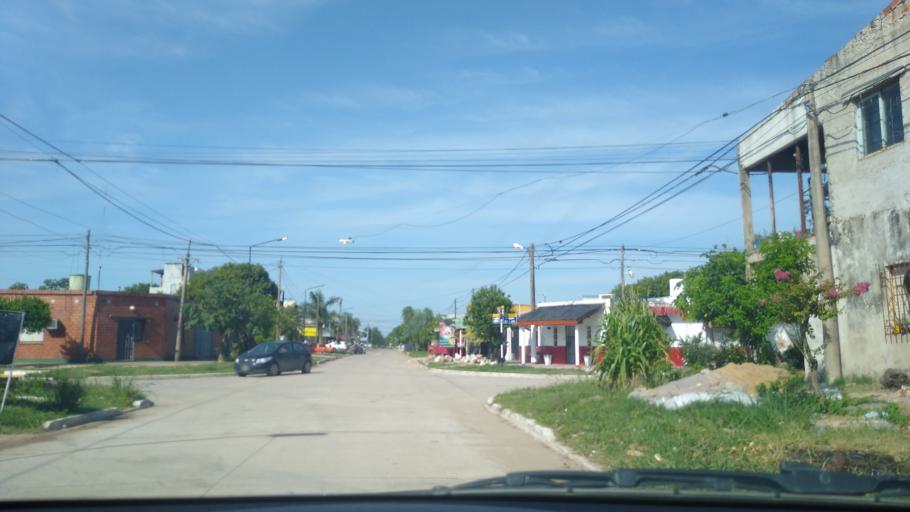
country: AR
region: Chaco
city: Barranqueras
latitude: -27.4841
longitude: -58.9479
